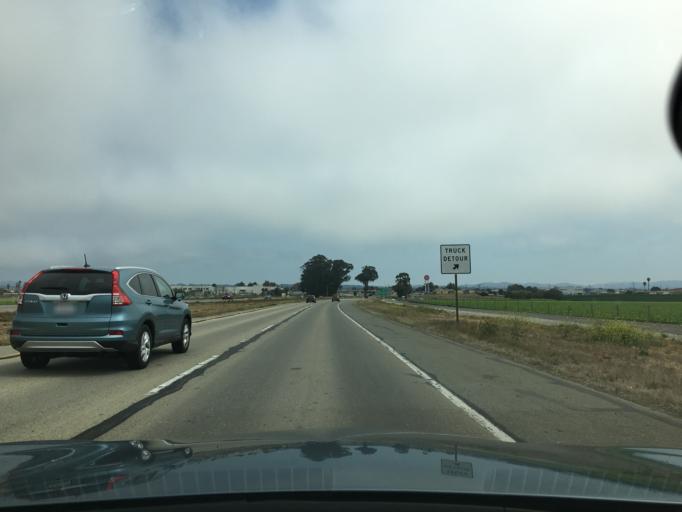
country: US
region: California
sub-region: Monterey County
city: Castroville
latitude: 36.7574
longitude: -121.7588
